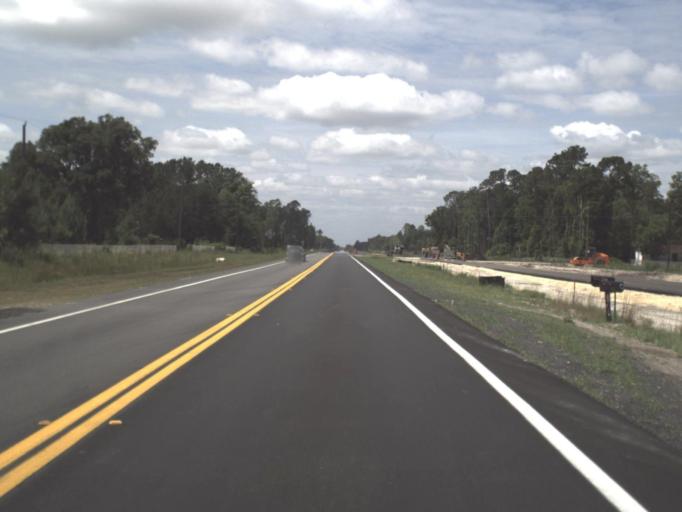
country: US
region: Florida
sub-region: Nassau County
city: Nassau Village-Ratliff
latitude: 30.4711
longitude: -81.9078
